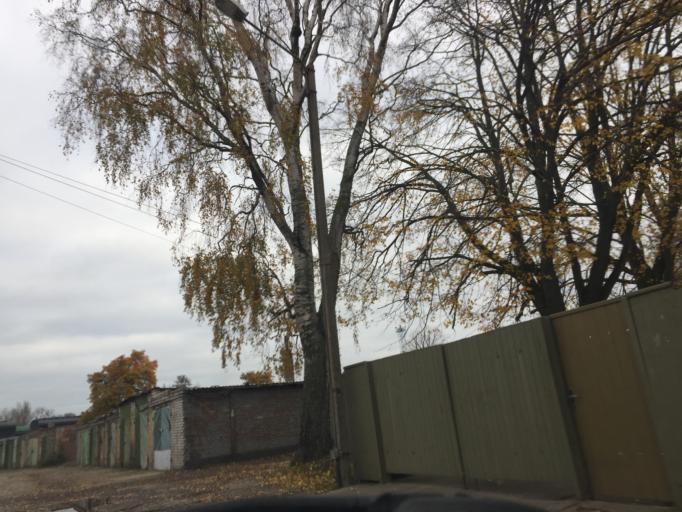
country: LV
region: Liepaja
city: Liepaja
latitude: 56.5222
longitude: 21.0136
